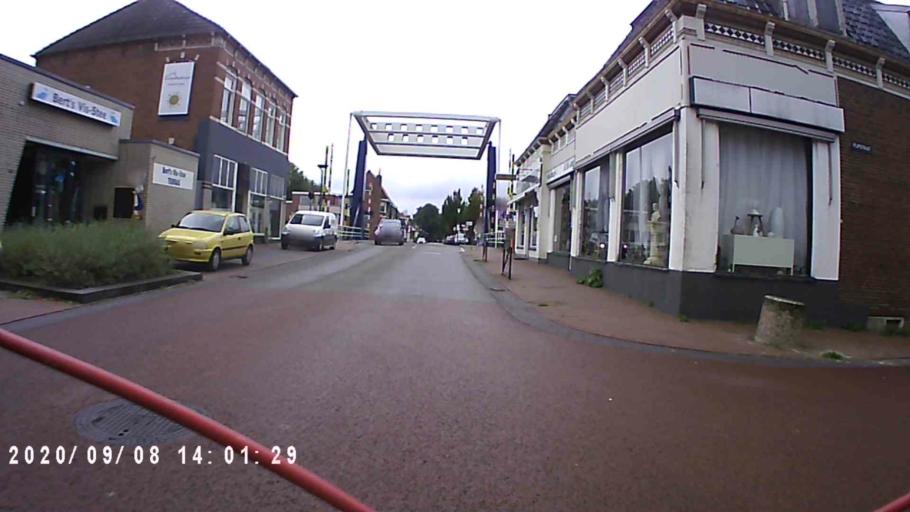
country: NL
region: Groningen
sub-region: Gemeente Veendam
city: Veendam
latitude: 53.1617
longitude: 6.8631
